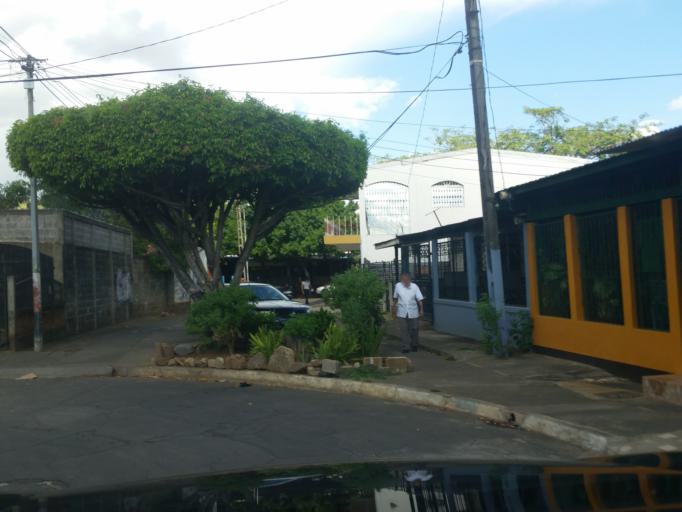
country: NI
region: Managua
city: Ciudad Sandino
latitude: 12.1538
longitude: -86.3022
